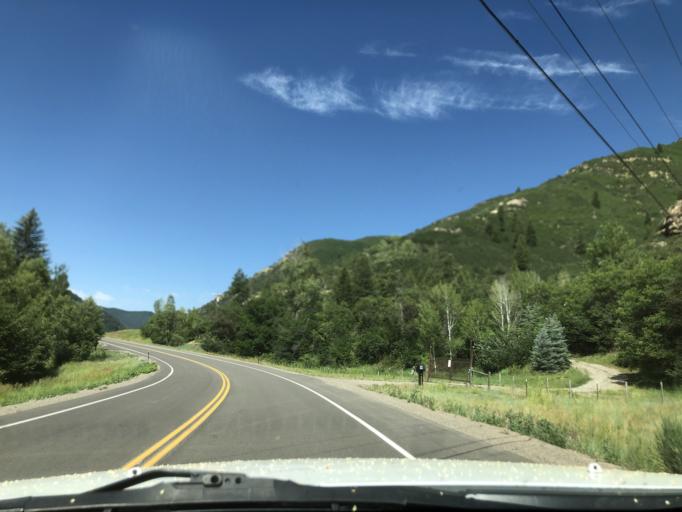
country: US
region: Colorado
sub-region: Delta County
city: Paonia
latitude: 38.9387
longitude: -107.3808
